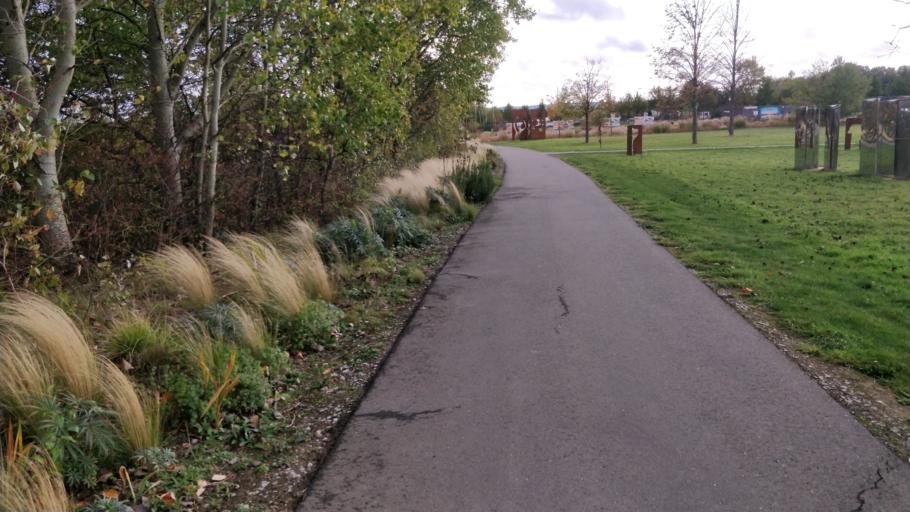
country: DE
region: North Rhine-Westphalia
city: Zulpich
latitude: 50.6791
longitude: 6.6555
